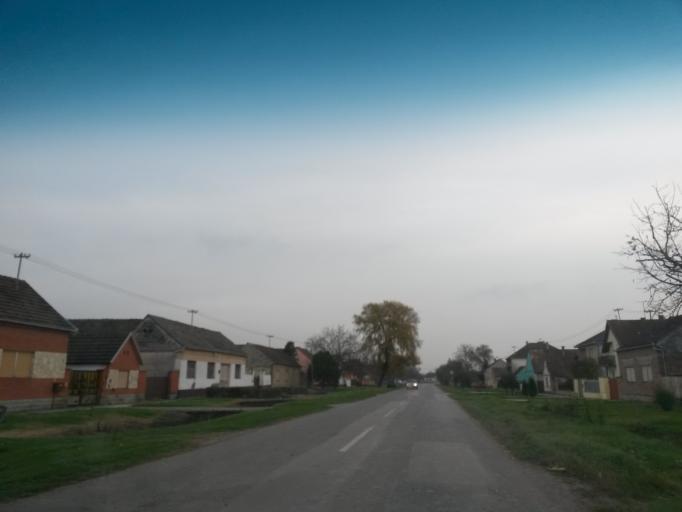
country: HR
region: Vukovarsko-Srijemska
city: Bobota
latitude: 45.4190
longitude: 18.8549
